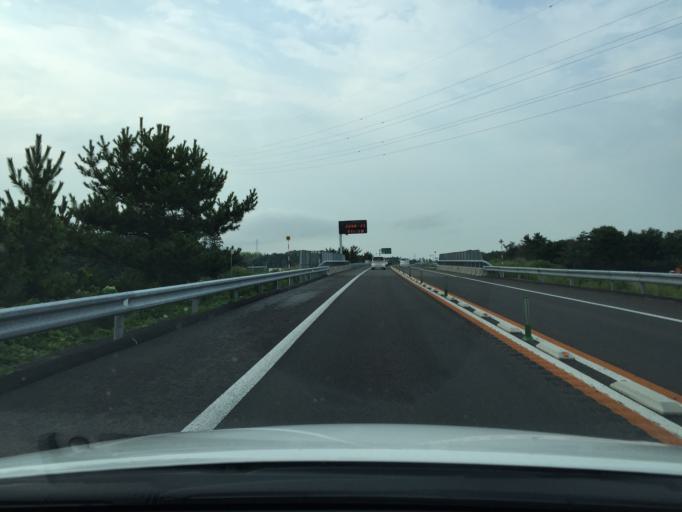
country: JP
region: Fukushima
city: Namie
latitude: 37.3700
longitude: 140.9671
